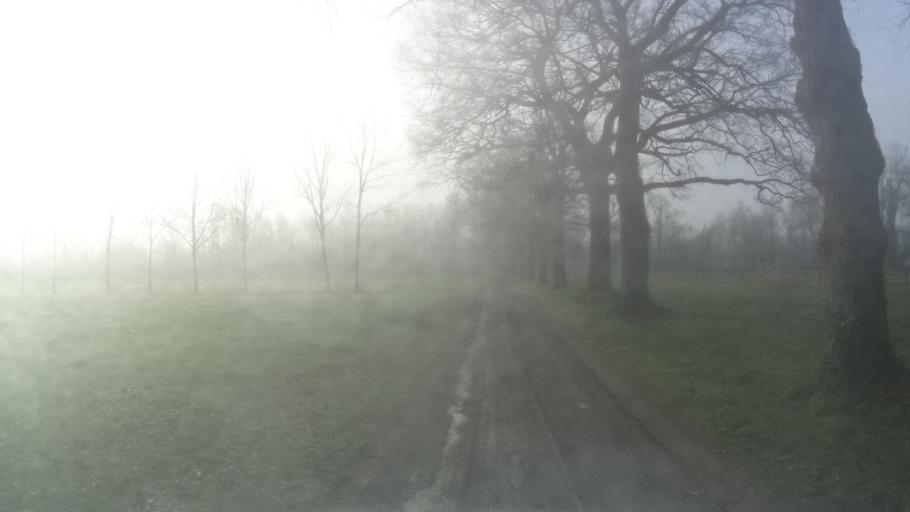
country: FR
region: Poitou-Charentes
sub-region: Departement de la Charente-Maritime
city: Saint-Aigulin
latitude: 45.1509
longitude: -0.0141
